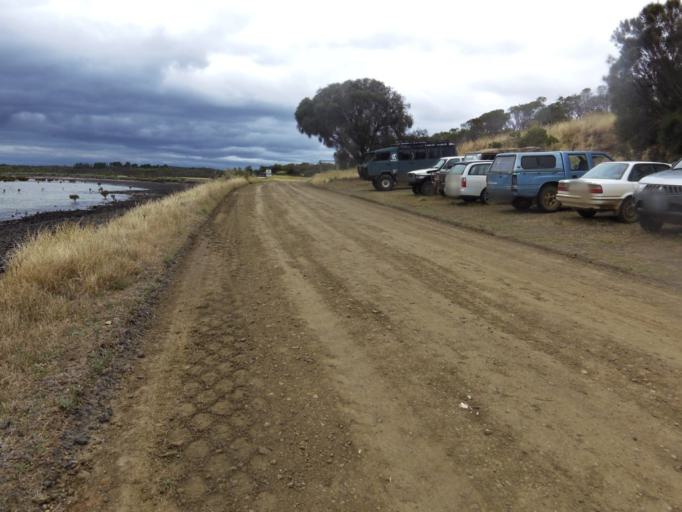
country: AU
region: Victoria
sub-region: Bass Coast
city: Cowes
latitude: -38.3825
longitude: 145.2739
